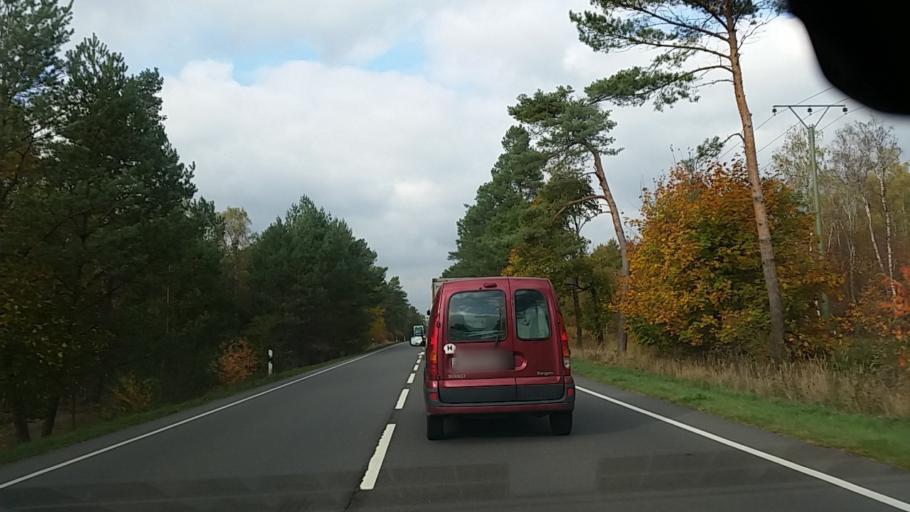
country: DE
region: Lower Saxony
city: Wesendorf
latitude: 52.5725
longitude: 10.5027
